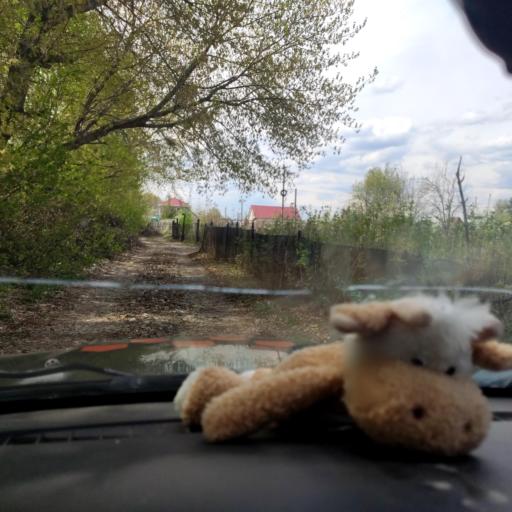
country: RU
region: Samara
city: Podstepki
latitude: 53.5105
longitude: 49.0850
